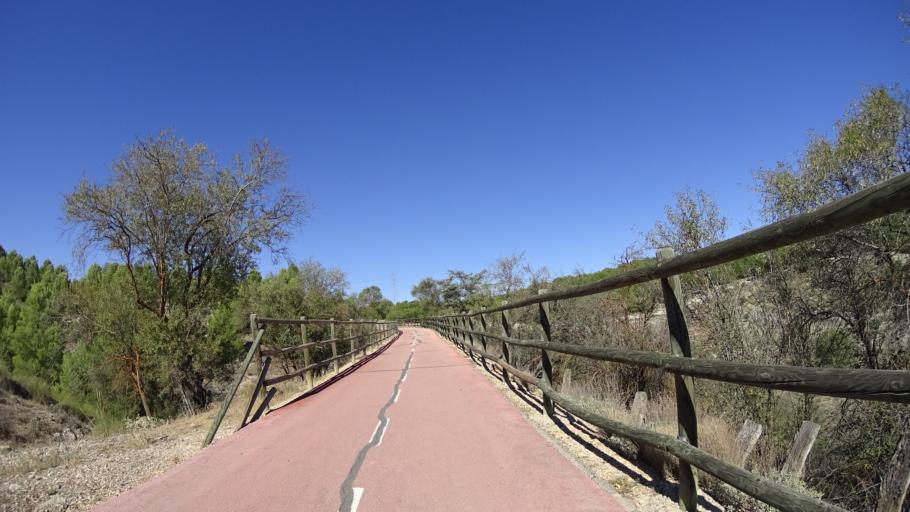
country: ES
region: Madrid
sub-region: Provincia de Madrid
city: Arganda
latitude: 40.2707
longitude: -3.4575
